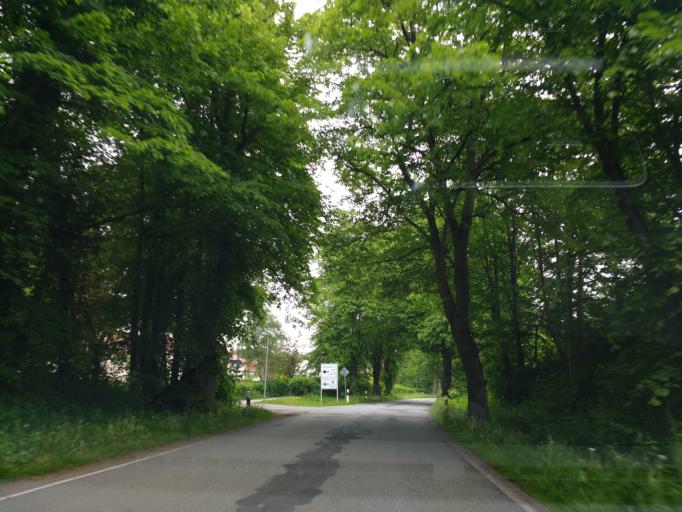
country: DE
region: Mecklenburg-Vorpommern
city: Neukloster
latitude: 53.8663
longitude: 11.6954
